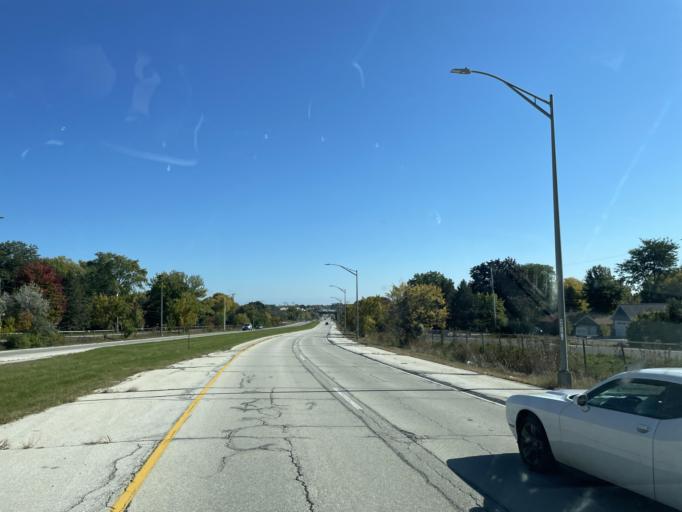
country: US
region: Wisconsin
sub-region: Waukesha County
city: Butler
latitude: 43.1304
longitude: -88.0501
